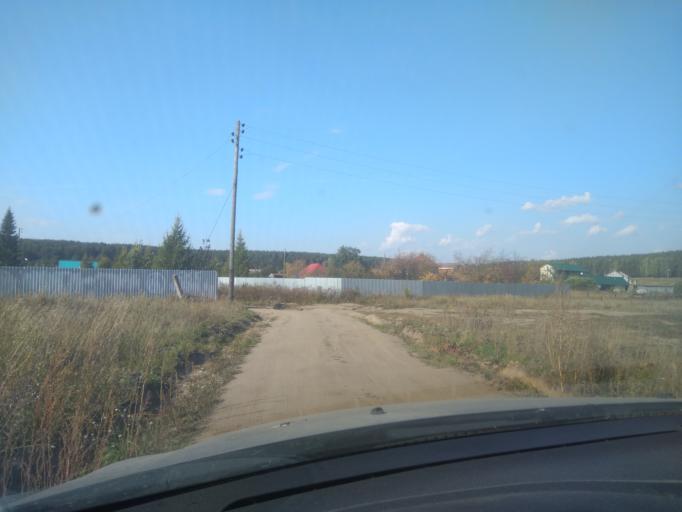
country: RU
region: Sverdlovsk
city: Pokrovskoye
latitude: 56.4356
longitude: 61.6018
